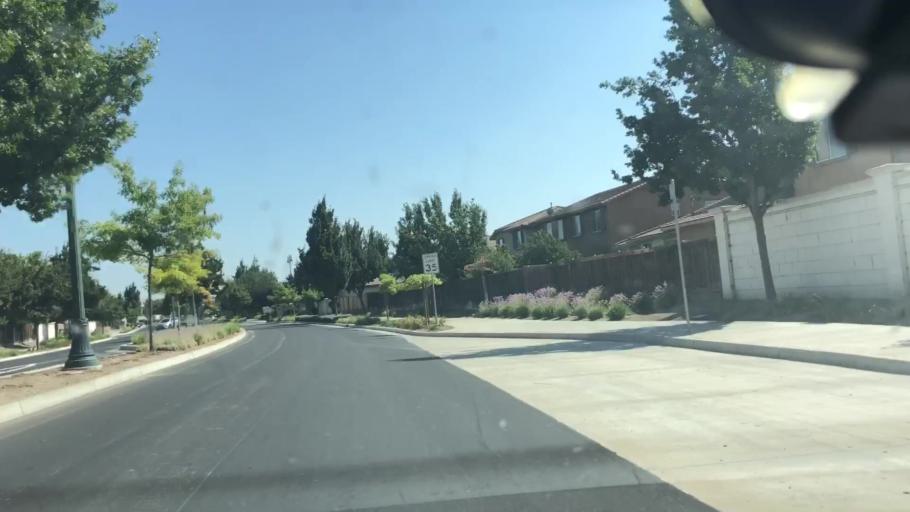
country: US
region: California
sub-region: San Joaquin County
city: Lathrop
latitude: 37.8105
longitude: -121.3065
